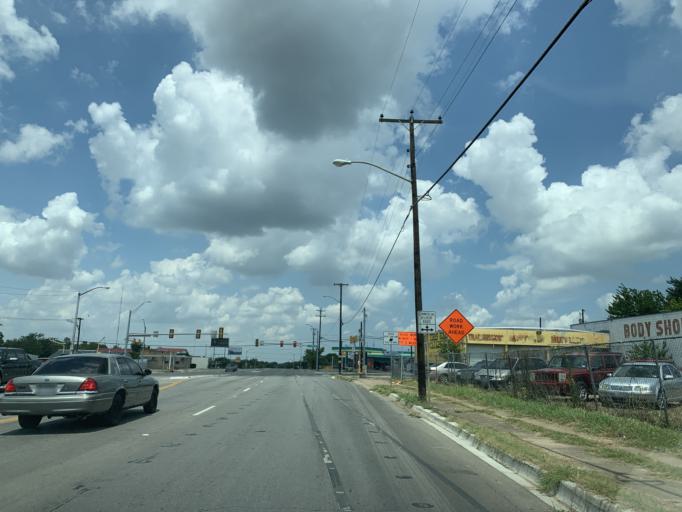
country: US
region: Texas
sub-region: Tarrant County
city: Forest Hill
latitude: 32.7303
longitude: -97.2619
